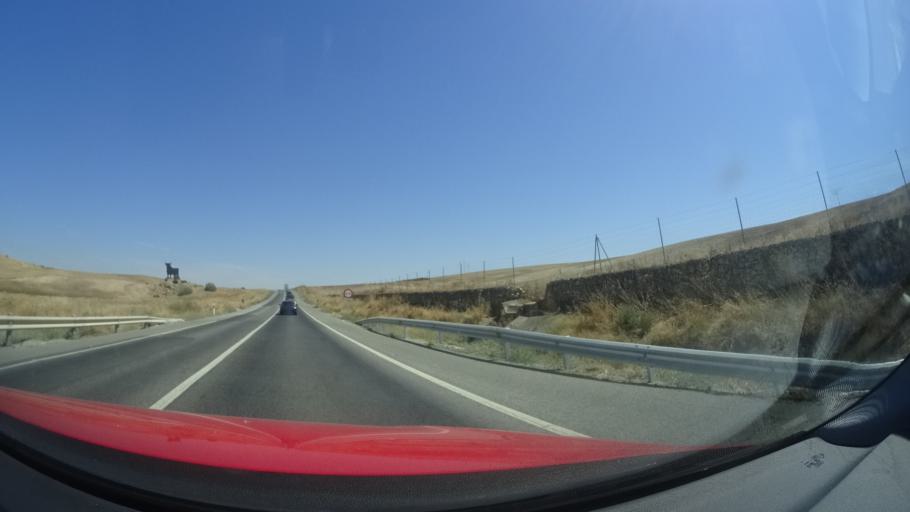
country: ES
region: Andalusia
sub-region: Provincia de Sevilla
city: Las Cabezas de San Juan
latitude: 36.9645
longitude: -5.8806
